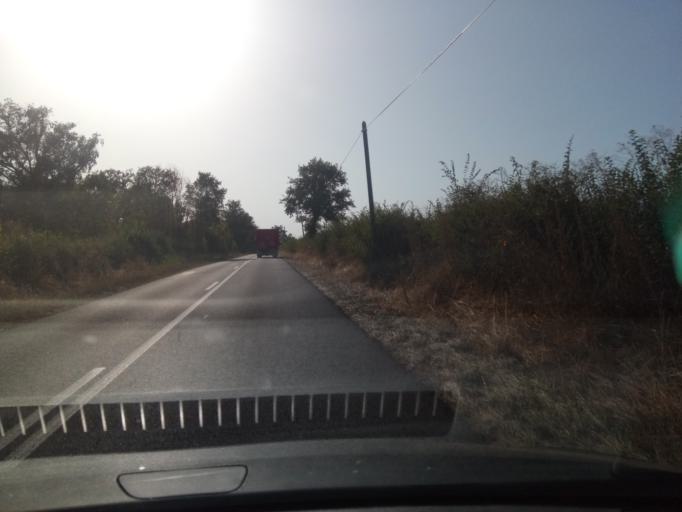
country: FR
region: Poitou-Charentes
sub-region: Departement de la Vienne
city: Lathus-Saint-Remy
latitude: 46.4491
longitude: 0.9955
